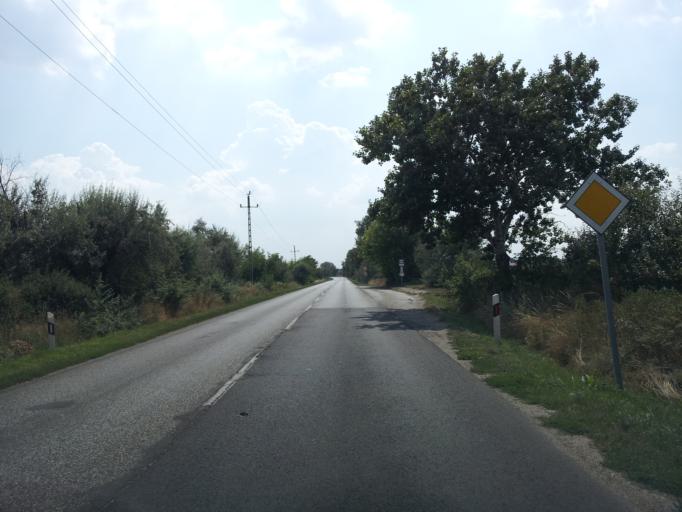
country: HU
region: Pest
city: Taksony
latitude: 47.3201
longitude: 19.0479
